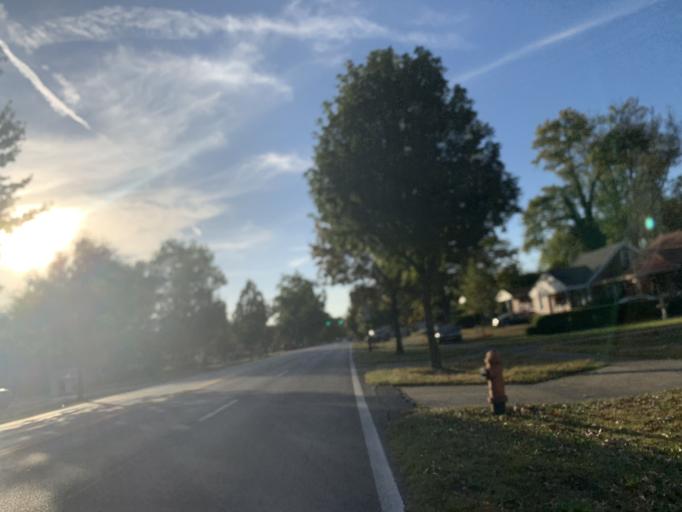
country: US
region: Kentucky
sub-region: Jefferson County
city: Shively
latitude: 38.2247
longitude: -85.8128
